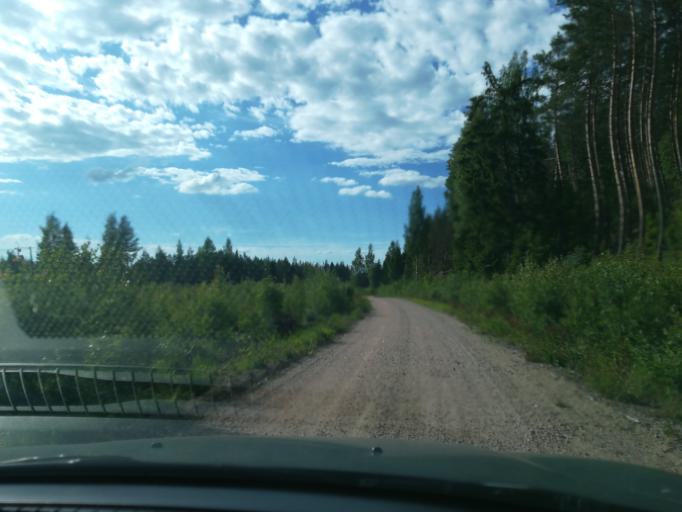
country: FI
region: Southern Savonia
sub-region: Savonlinna
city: Savonlinna
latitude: 61.6406
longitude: 28.7220
